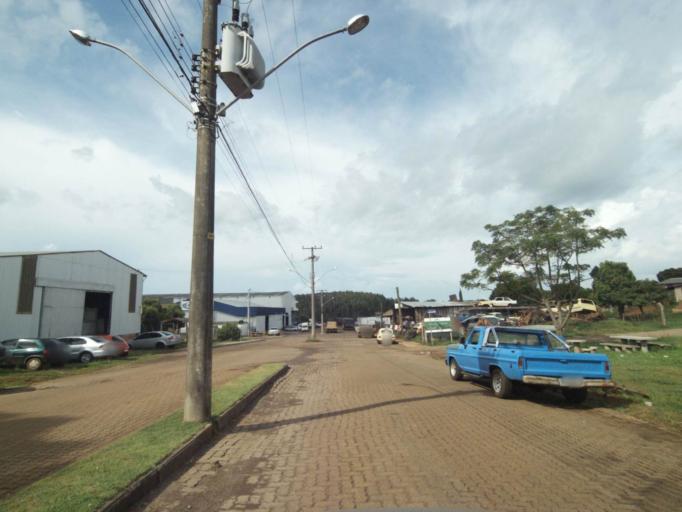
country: BR
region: Rio Grande do Sul
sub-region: Lagoa Vermelha
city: Lagoa Vermelha
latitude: -28.2296
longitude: -51.5153
